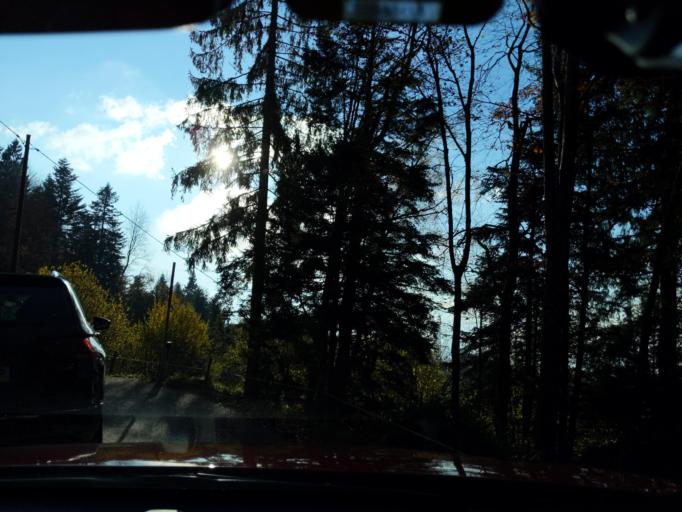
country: AT
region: Vorarlberg
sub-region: Politischer Bezirk Bregenz
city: Eichenberg
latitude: 47.5186
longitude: 9.7774
